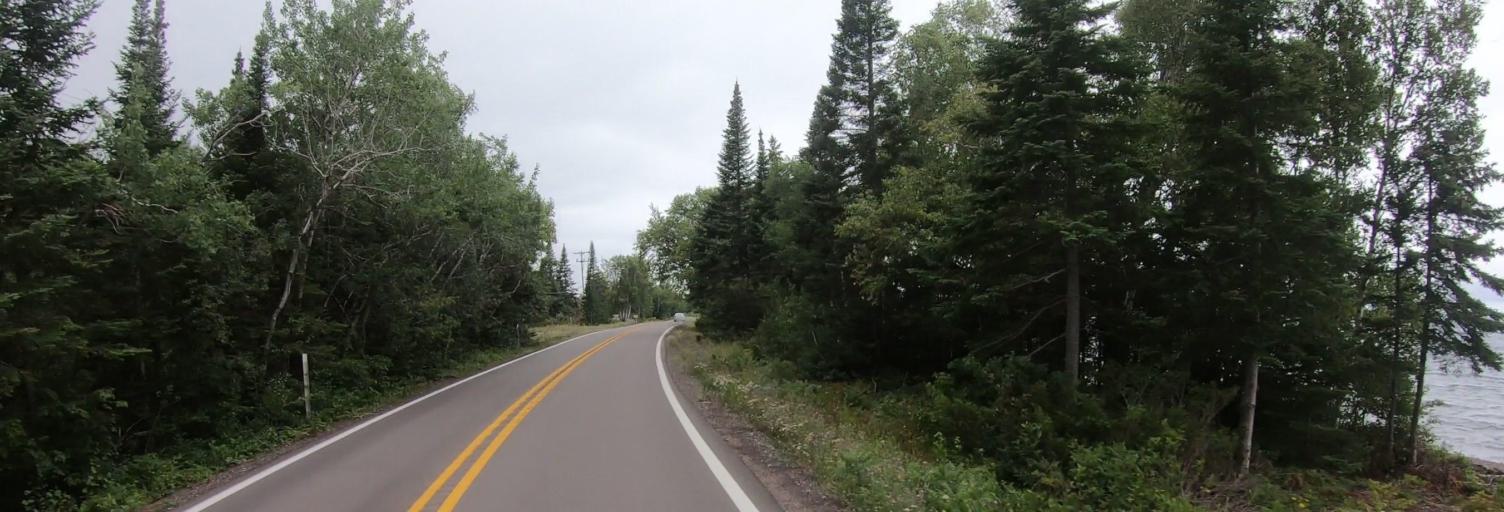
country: US
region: Michigan
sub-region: Keweenaw County
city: Eagle River
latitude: 47.4788
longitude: -87.9608
